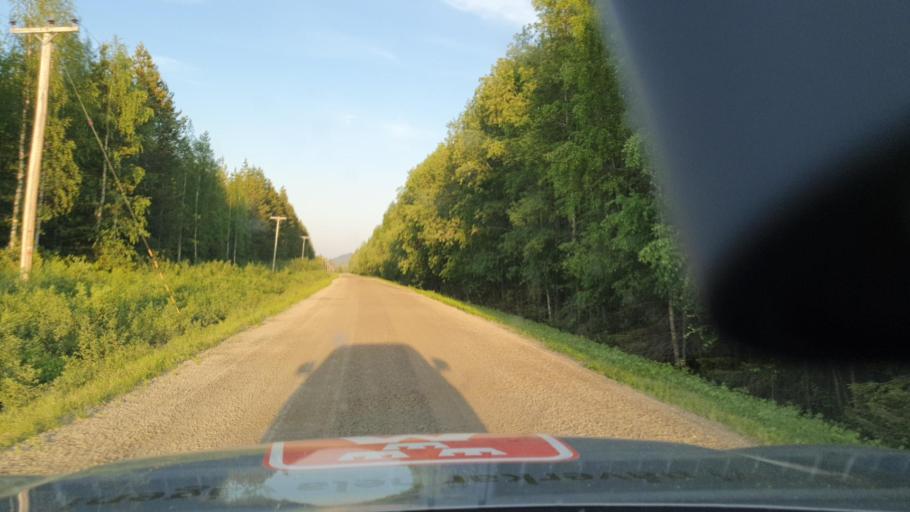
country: SE
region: Norrbotten
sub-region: Bodens Kommun
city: Boden
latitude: 66.1772
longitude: 21.5115
